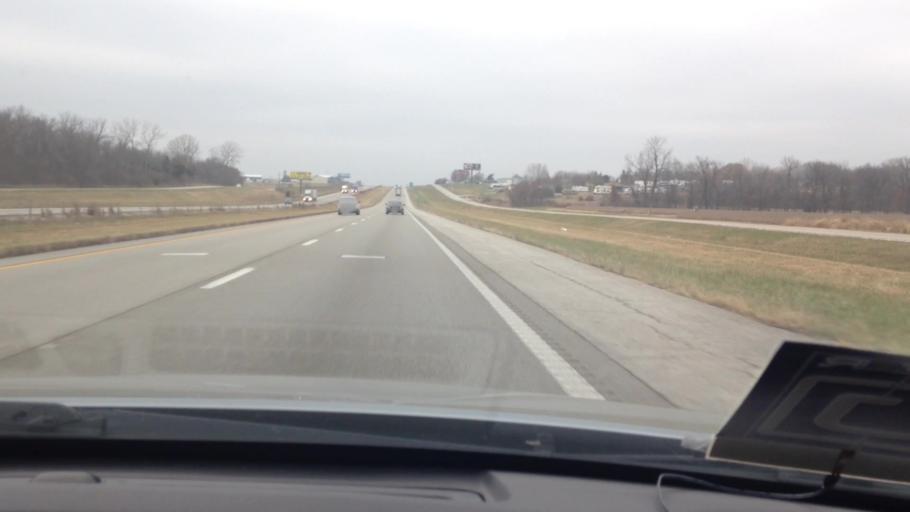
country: US
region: Missouri
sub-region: Cass County
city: Peculiar
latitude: 38.7017
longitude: -94.4347
